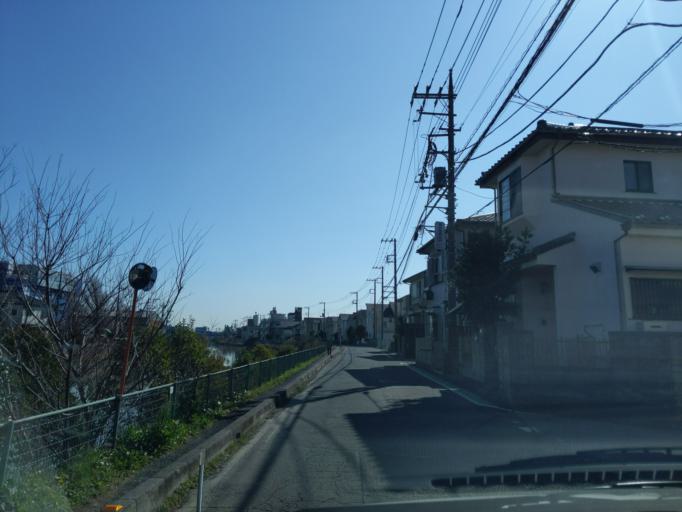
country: JP
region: Saitama
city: Soka
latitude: 35.8330
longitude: 139.8102
